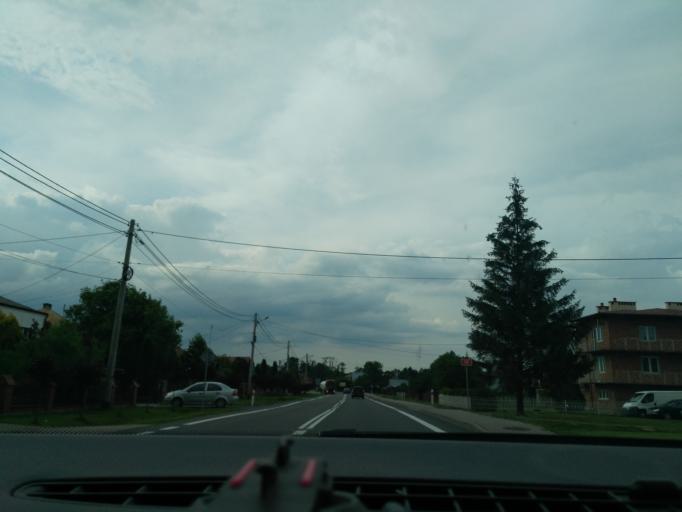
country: PL
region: Subcarpathian Voivodeship
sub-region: Powiat rzeszowski
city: Kamien
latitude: 50.3396
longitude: 22.1357
